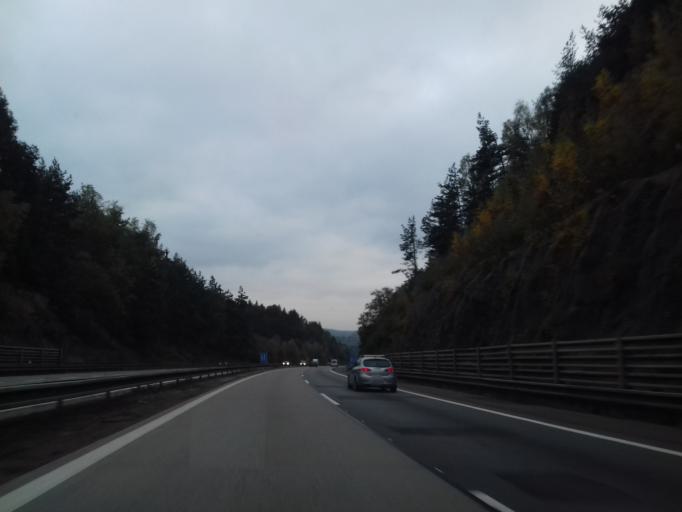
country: CZ
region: Central Bohemia
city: Ondrejov
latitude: 49.8867
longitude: 14.7556
